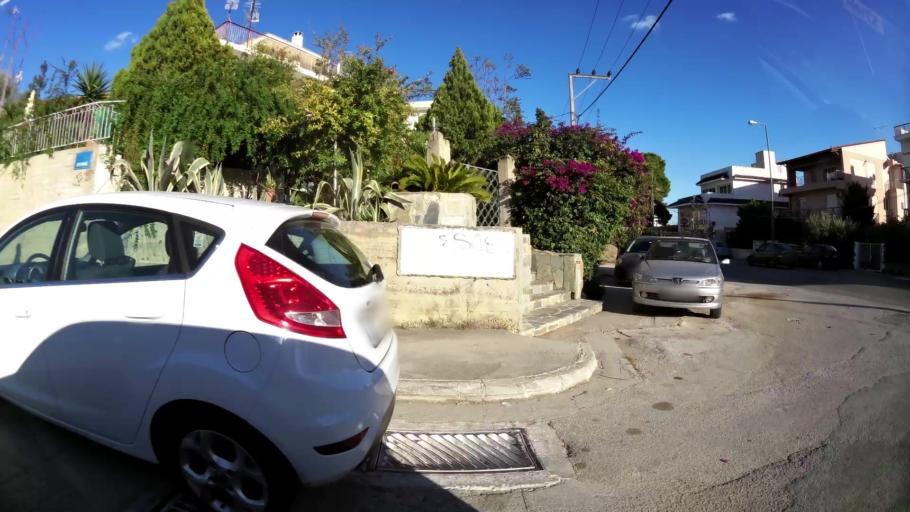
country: GR
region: Attica
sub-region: Nomarchia Anatolikis Attikis
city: Rafina
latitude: 38.0190
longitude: 23.9994
